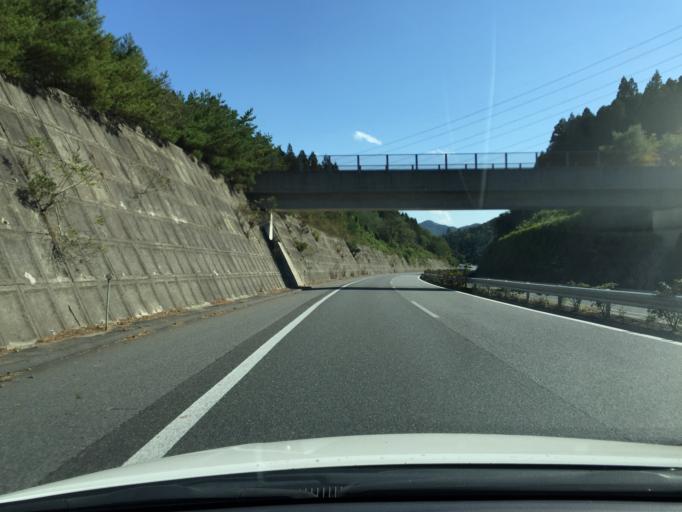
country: JP
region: Fukushima
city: Iwaki
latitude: 37.1505
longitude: 140.7400
